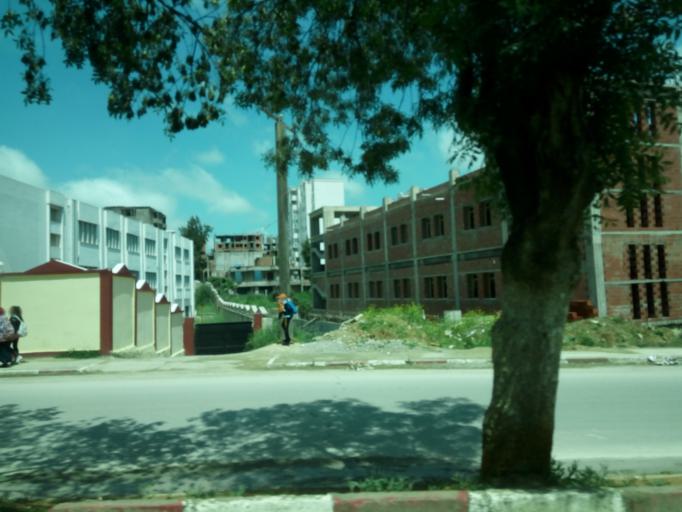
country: DZ
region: Tipaza
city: Saoula
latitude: 36.7307
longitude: 2.9965
